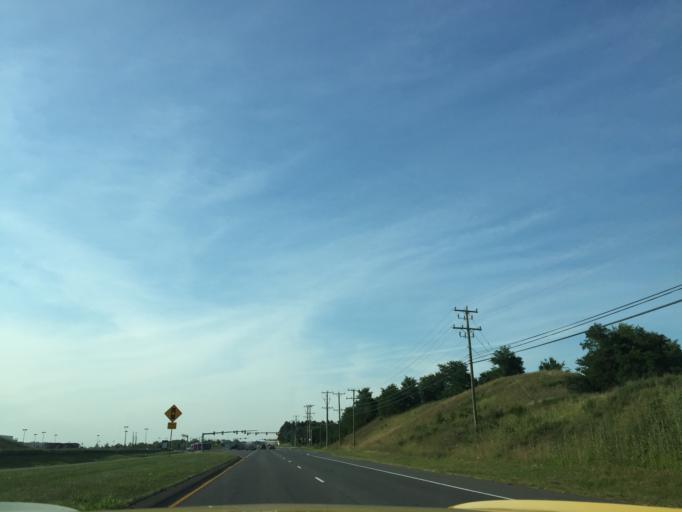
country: US
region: Virginia
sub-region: Loudoun County
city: University Center
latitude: 39.0476
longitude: -77.4506
